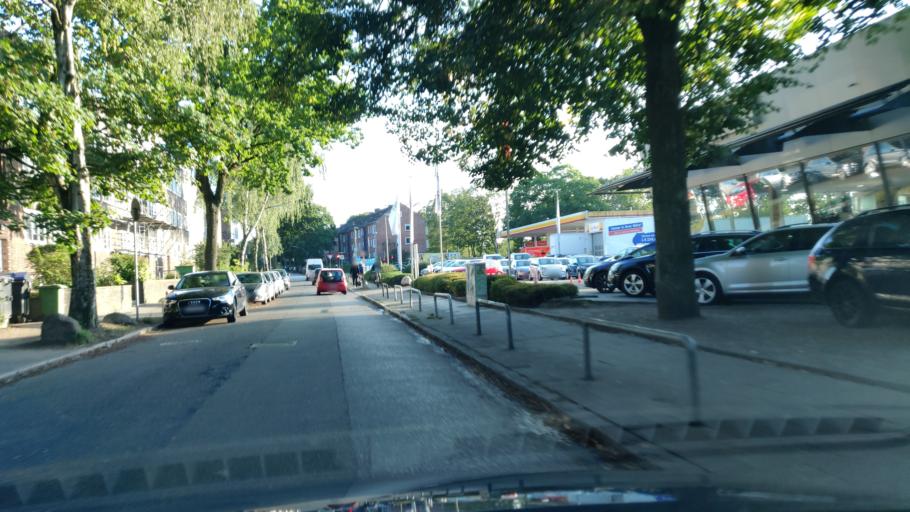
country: DE
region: Hamburg
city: Altona
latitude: 53.5555
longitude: 9.9102
